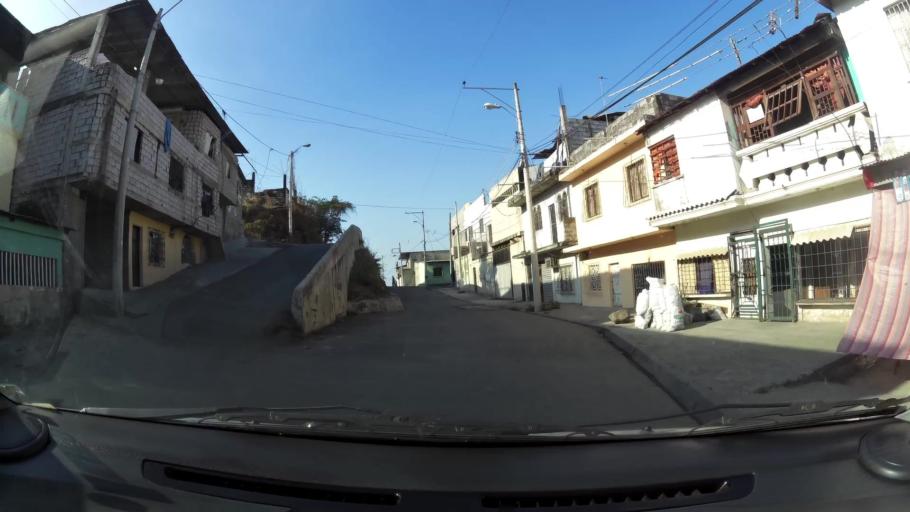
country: EC
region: Guayas
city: Guayaquil
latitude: -2.1556
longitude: -79.9149
